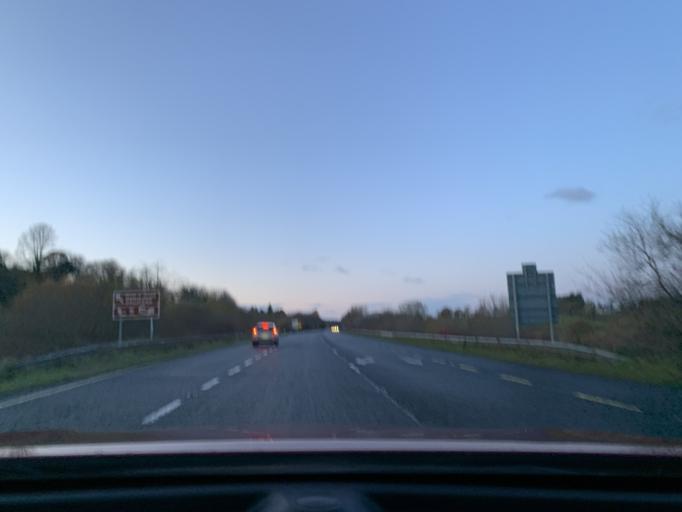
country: IE
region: Connaught
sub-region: County Leitrim
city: Carrick-on-Shannon
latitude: 53.9266
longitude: -7.9979
